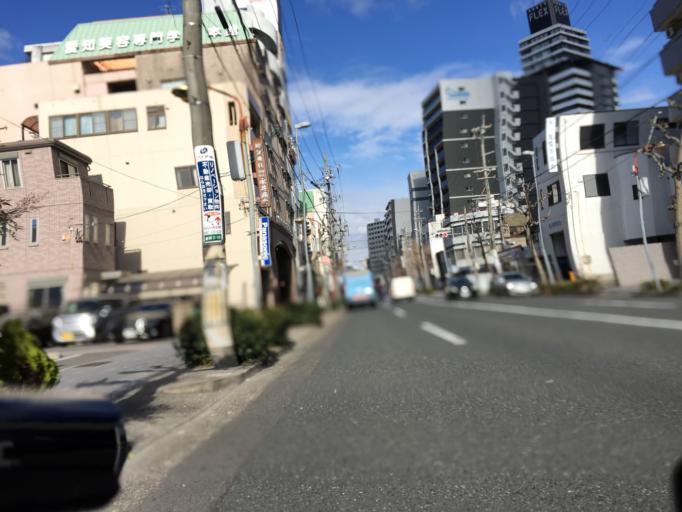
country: JP
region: Aichi
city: Nagoya-shi
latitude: 35.1679
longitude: 136.9219
